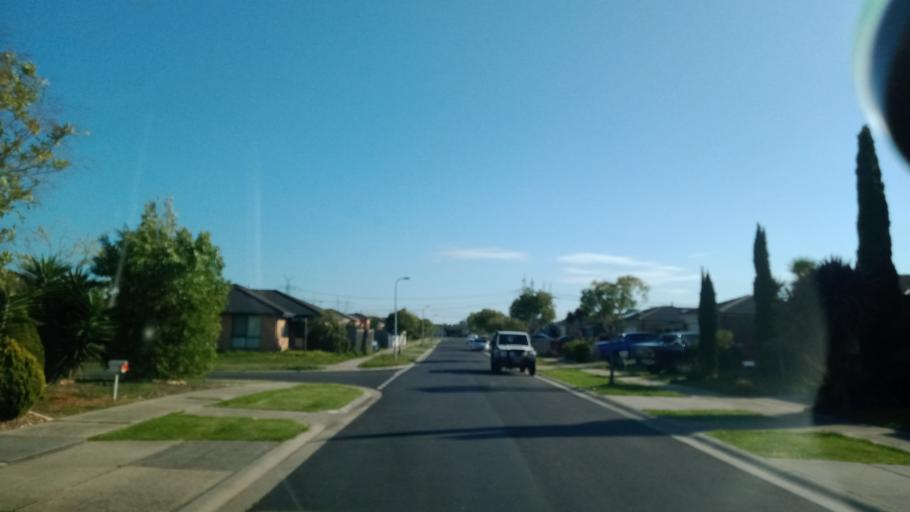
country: AU
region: Victoria
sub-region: Casey
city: Cranbourne West
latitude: -38.0915
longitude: 145.2679
